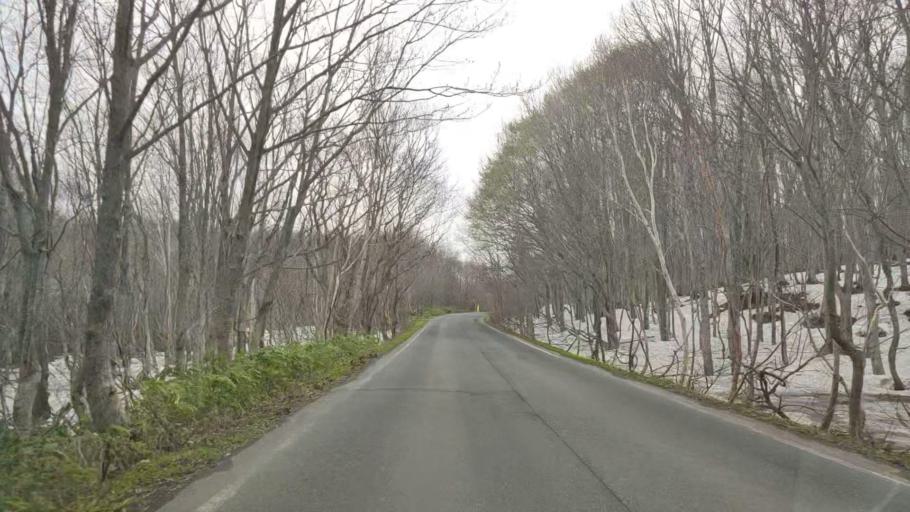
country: JP
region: Aomori
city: Aomori Shi
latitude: 40.6805
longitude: 140.9349
